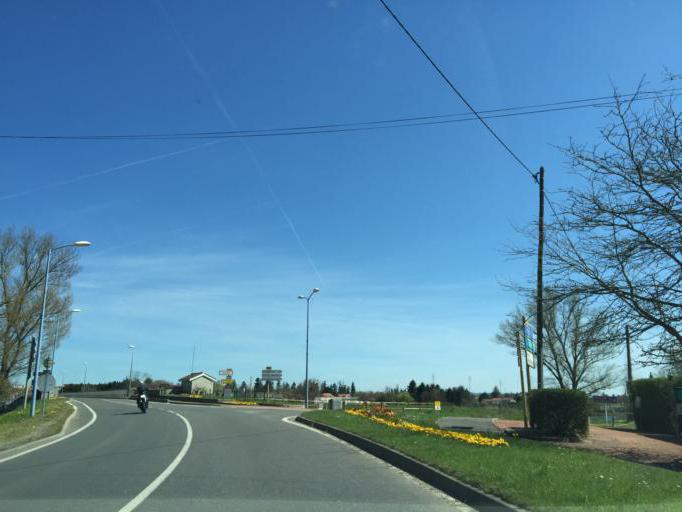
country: FR
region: Rhone-Alpes
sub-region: Departement de la Loire
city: Feurs
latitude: 45.7424
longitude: 4.2096
